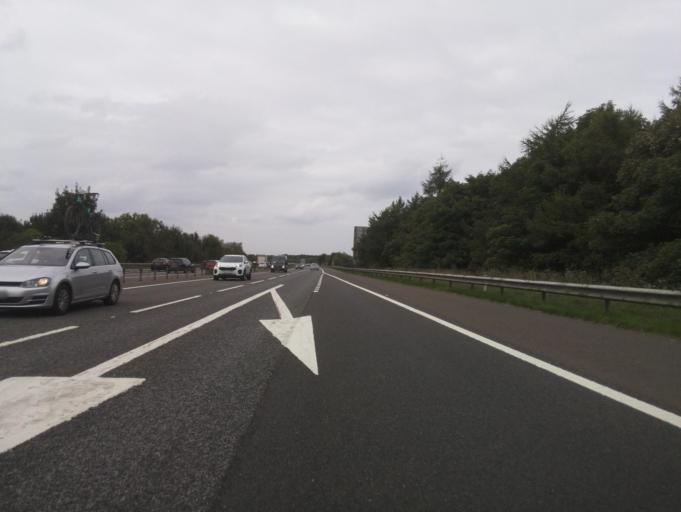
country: GB
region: England
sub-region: County Durham
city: West Rainton
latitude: 54.7978
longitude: -1.5258
